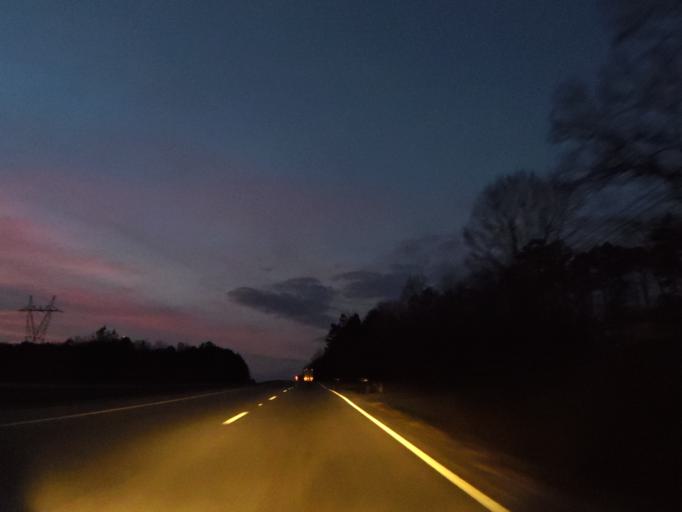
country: US
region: Tennessee
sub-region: Bradley County
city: East Cleveland
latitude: 35.1394
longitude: -84.7818
